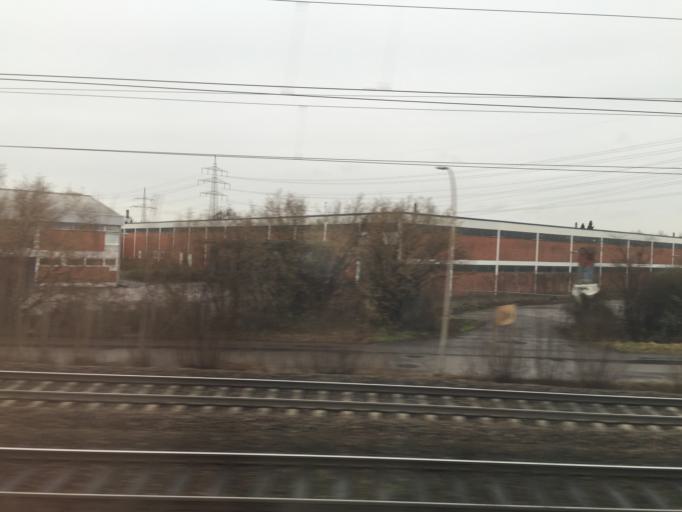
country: DE
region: Baden-Wuerttemberg
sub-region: Regierungsbezirk Stuttgart
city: Tamm
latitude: 48.9275
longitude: 9.1224
